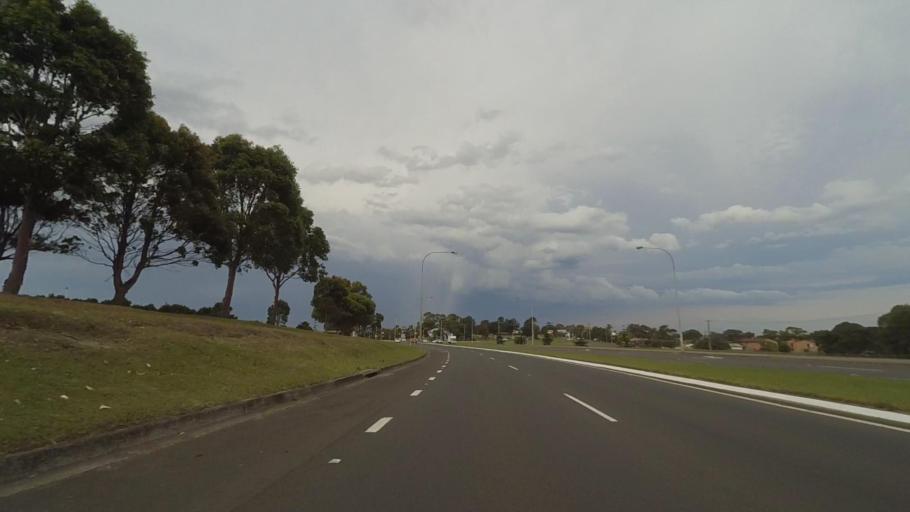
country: AU
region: New South Wales
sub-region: Shellharbour
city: Flinders
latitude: -34.5825
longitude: 150.8596
